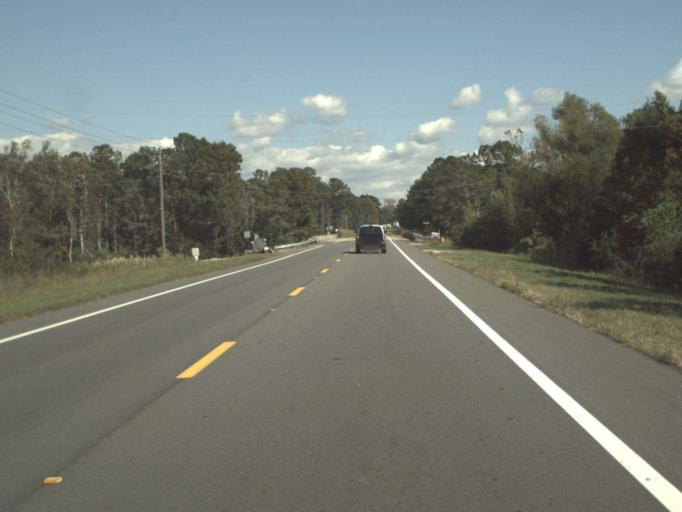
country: US
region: Florida
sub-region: Walton County
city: Freeport
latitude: 30.5121
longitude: -86.1880
